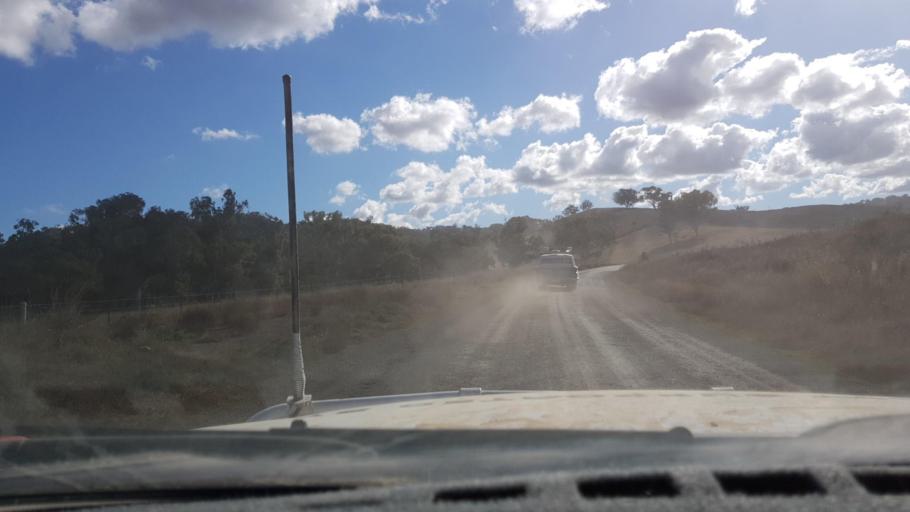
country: AU
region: New South Wales
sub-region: Tamworth Municipality
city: Manilla
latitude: -30.6158
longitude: 150.5144
